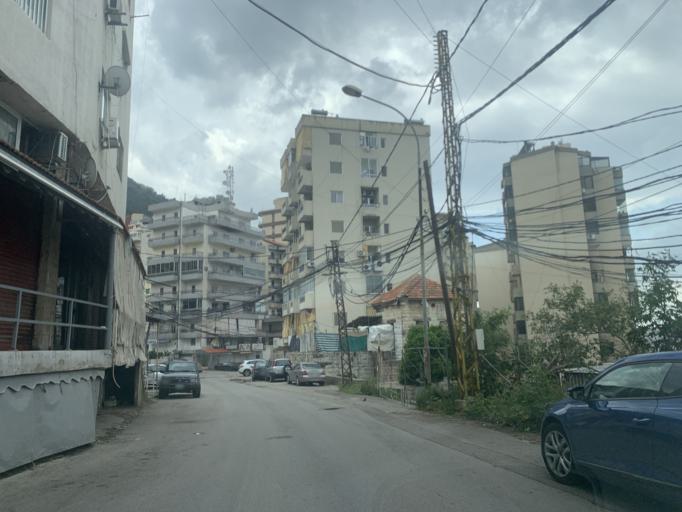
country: LB
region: Mont-Liban
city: Djounie
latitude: 33.9868
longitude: 35.6431
